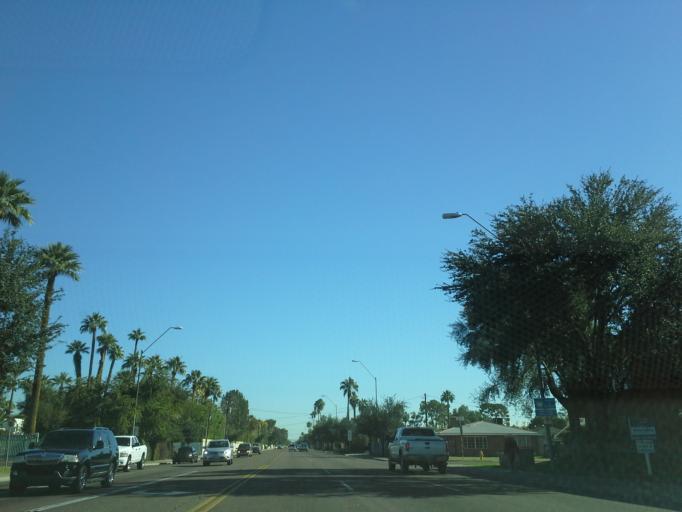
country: US
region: Arizona
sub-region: Maricopa County
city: Phoenix
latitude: 33.4802
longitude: -112.0646
